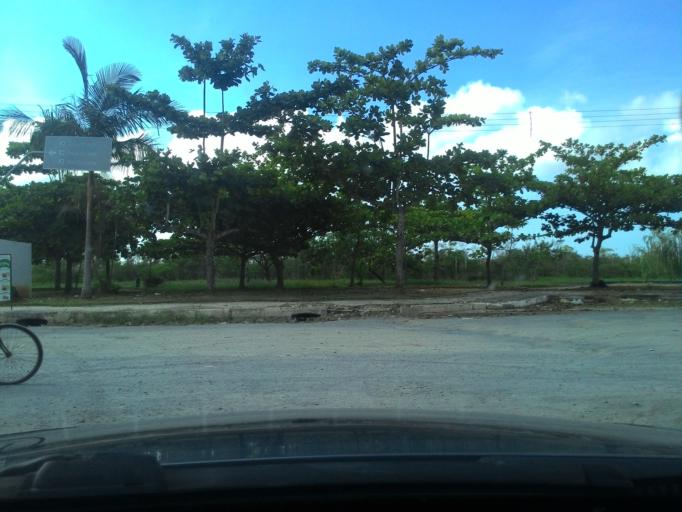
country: BR
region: Sao Paulo
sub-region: Iguape
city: Iguape
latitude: -24.7114
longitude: -47.5573
